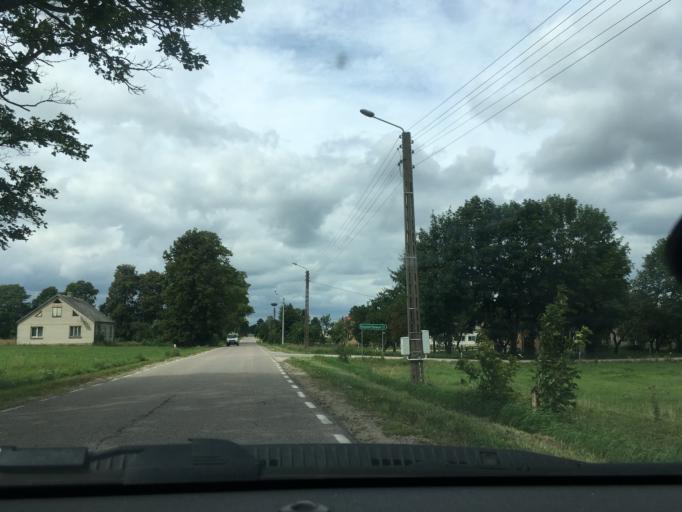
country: PL
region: Podlasie
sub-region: Powiat suwalski
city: Raczki
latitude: 53.9600
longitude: 22.8206
